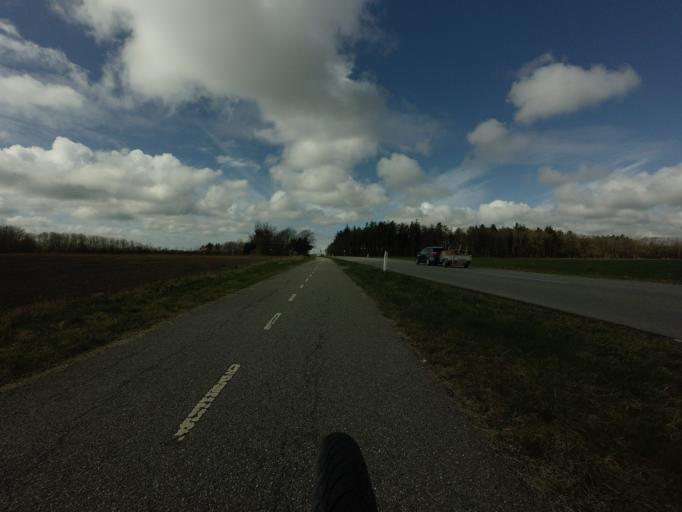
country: DK
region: North Denmark
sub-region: Hjorring Kommune
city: Vra
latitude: 57.3561
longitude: 9.8871
